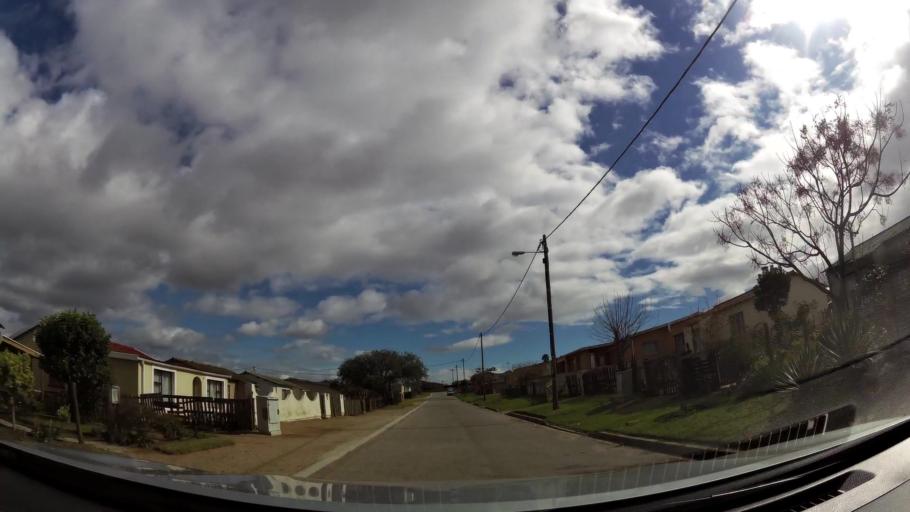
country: ZA
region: Western Cape
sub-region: Eden District Municipality
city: George
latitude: -34.0225
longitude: 22.4720
